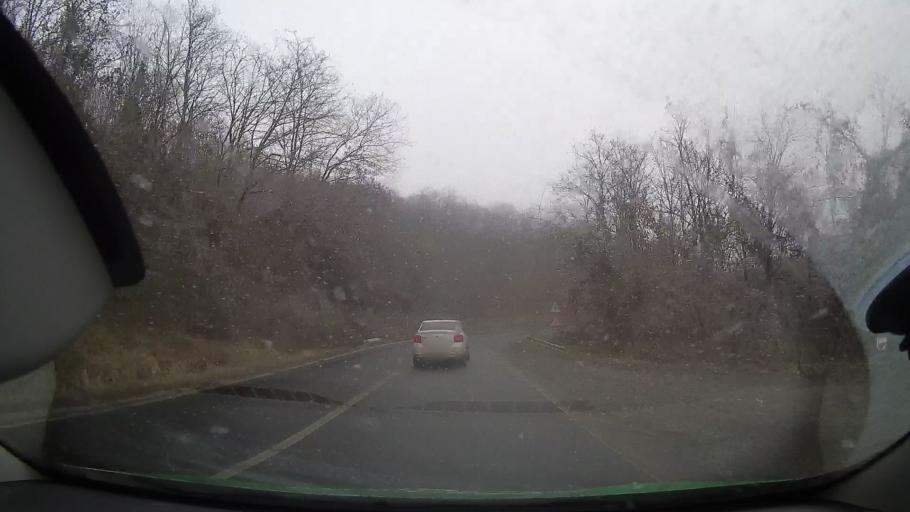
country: RO
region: Sibiu
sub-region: Municipiul Medias
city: Medias
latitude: 46.1856
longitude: 24.3320
